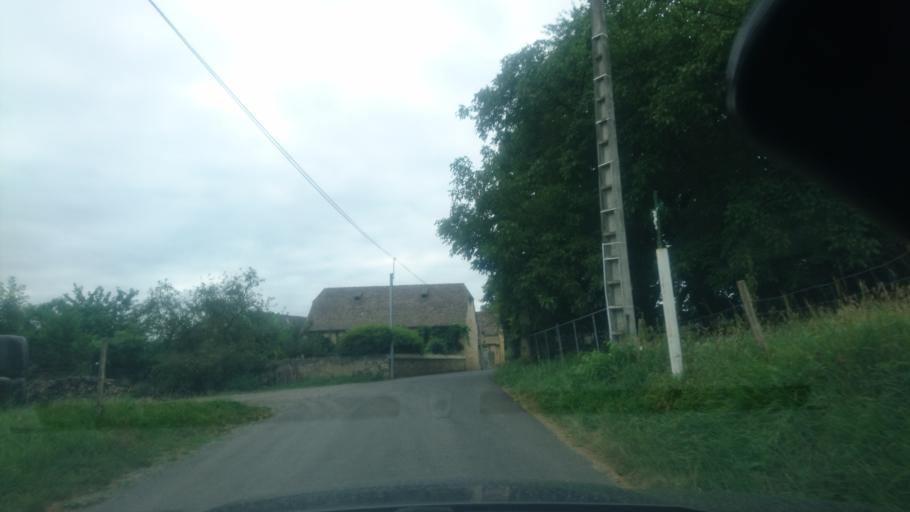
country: FR
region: Midi-Pyrenees
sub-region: Departement des Hautes-Pyrenees
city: Horgues
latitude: 43.1212
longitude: 0.0660
